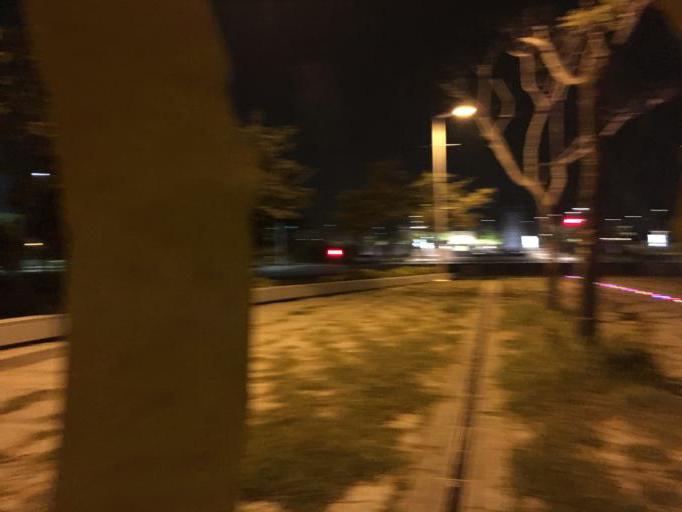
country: TW
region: Taiwan
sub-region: Chiayi
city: Taibao
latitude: 23.4685
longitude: 120.2941
